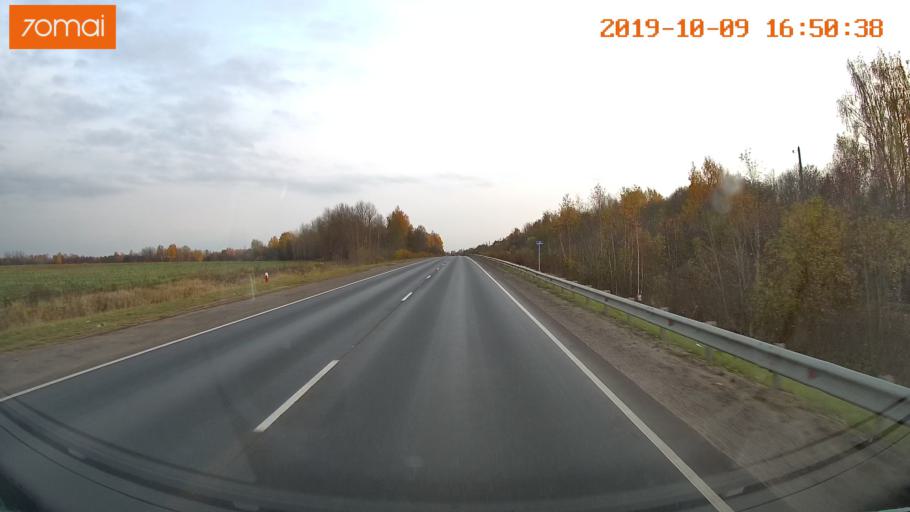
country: RU
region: Kostroma
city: Volgorechensk
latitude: 57.3982
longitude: 41.2114
